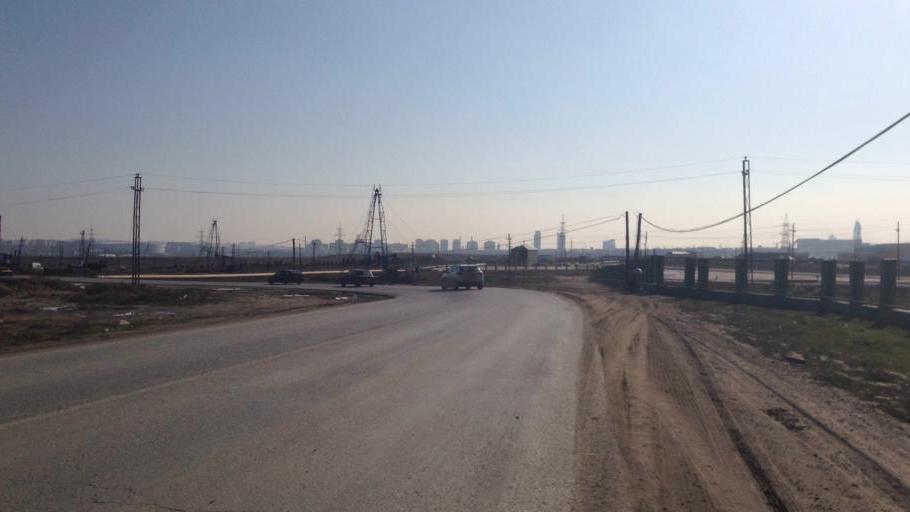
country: AZ
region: Baki
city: Balakhani
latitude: 40.4578
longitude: 49.8915
